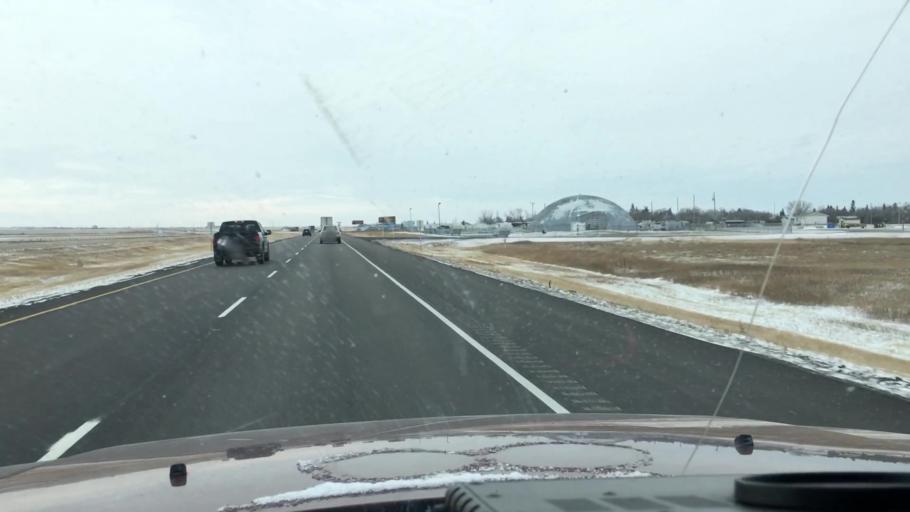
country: CA
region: Saskatchewan
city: Saskatoon
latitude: 51.8185
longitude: -106.4989
